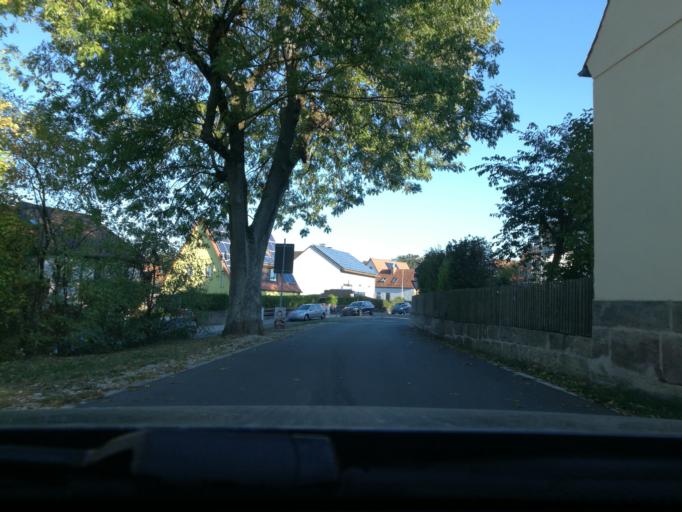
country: DE
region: Bavaria
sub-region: Regierungsbezirk Mittelfranken
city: Cadolzburg
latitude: 49.4613
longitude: 10.8532
